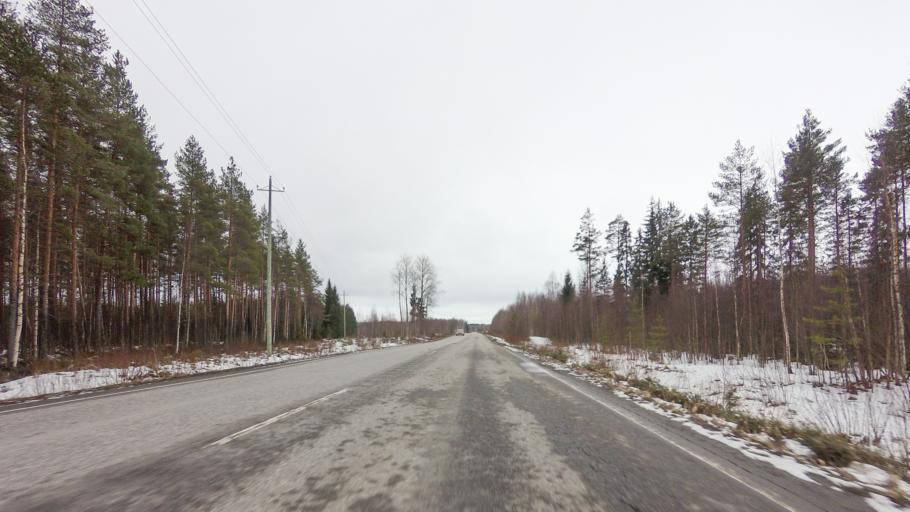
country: FI
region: Southern Savonia
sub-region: Savonlinna
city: Savonlinna
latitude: 61.9034
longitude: 28.9267
